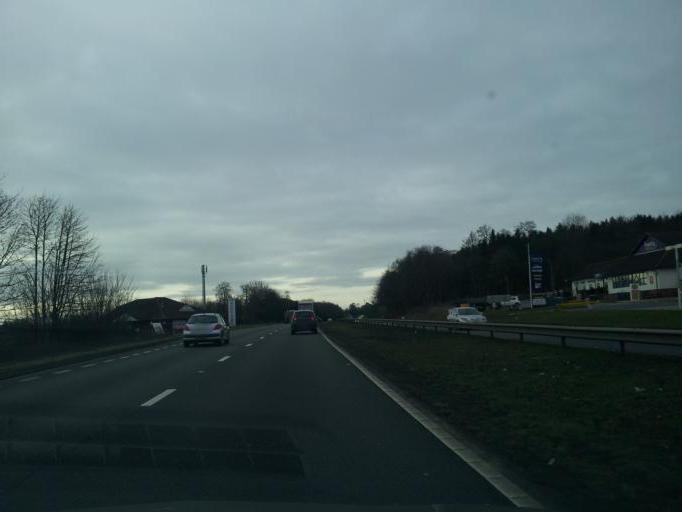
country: GB
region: England
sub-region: Lincolnshire
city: Grantham
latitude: 52.8386
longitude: -0.6290
